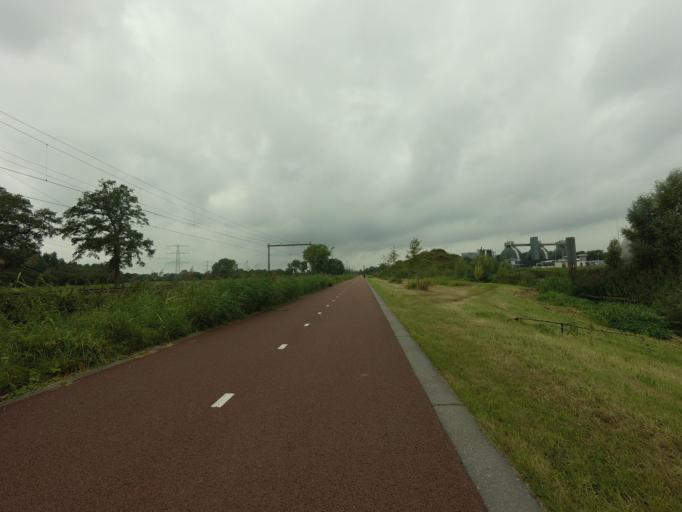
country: NL
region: Overijssel
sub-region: Gemeente Hengelo
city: Hengelo
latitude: 52.2780
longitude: 6.7695
